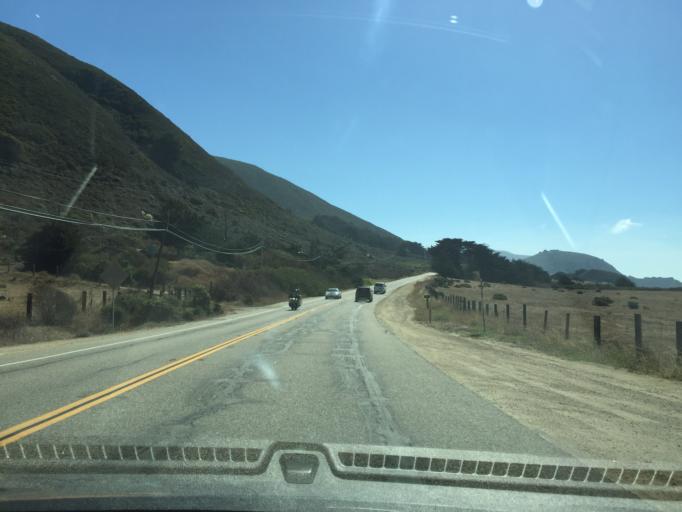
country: US
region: California
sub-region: Monterey County
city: Carmel-by-the-Sea
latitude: 36.3984
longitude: -121.9039
